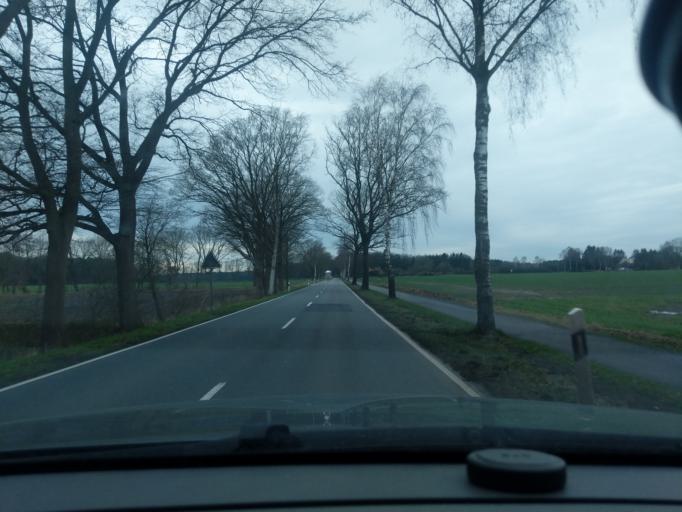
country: DE
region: Lower Saxony
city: Lauenbruck
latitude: 53.1526
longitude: 9.5373
